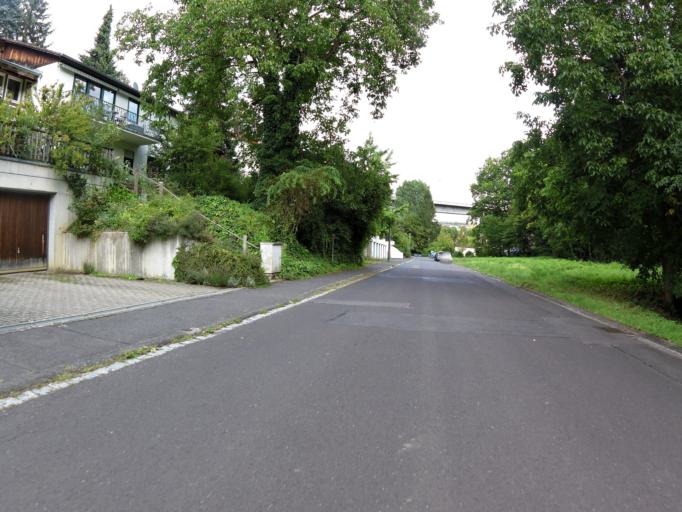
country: DE
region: Bavaria
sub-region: Regierungsbezirk Unterfranken
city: Margetshochheim
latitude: 49.8280
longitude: 9.8624
